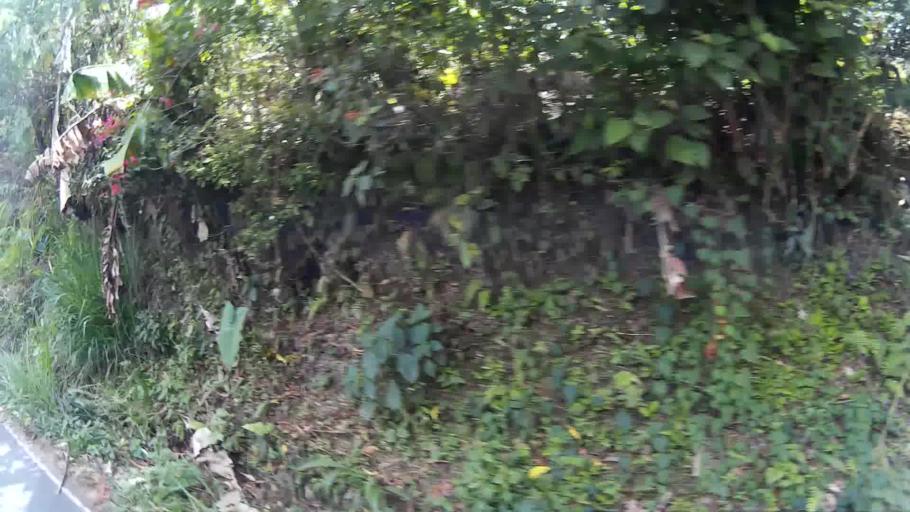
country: CO
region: Risaralda
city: Marsella
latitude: 4.8972
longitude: -75.7458
